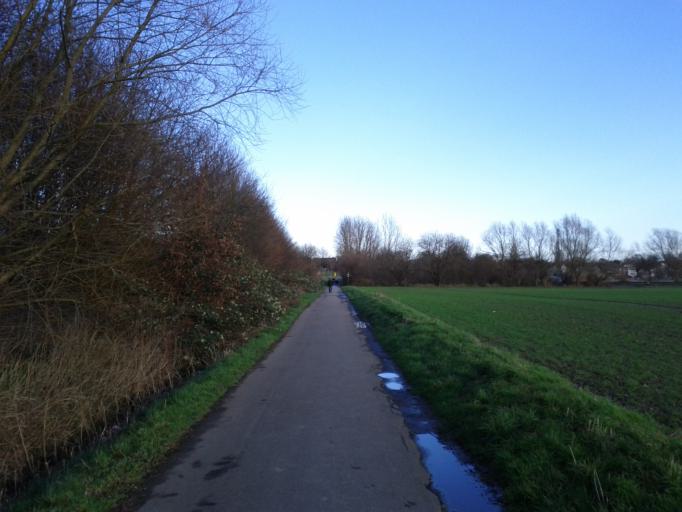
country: DE
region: North Rhine-Westphalia
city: Lanstrop
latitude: 51.5609
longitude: 7.5428
